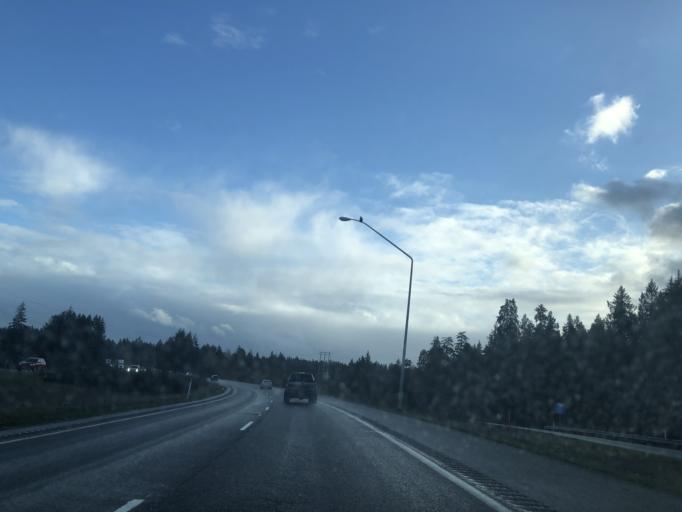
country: US
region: Washington
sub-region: Kitsap County
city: Chico
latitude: 47.6056
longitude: -122.7119
